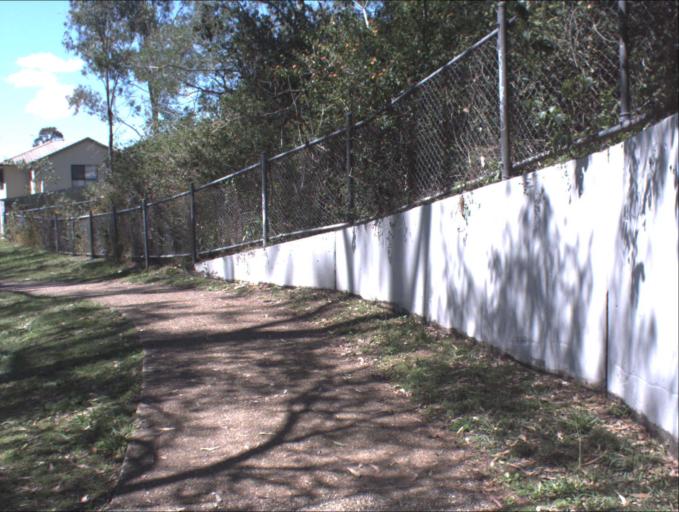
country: AU
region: Queensland
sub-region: Logan
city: Beenleigh
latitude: -27.7040
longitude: 153.1715
